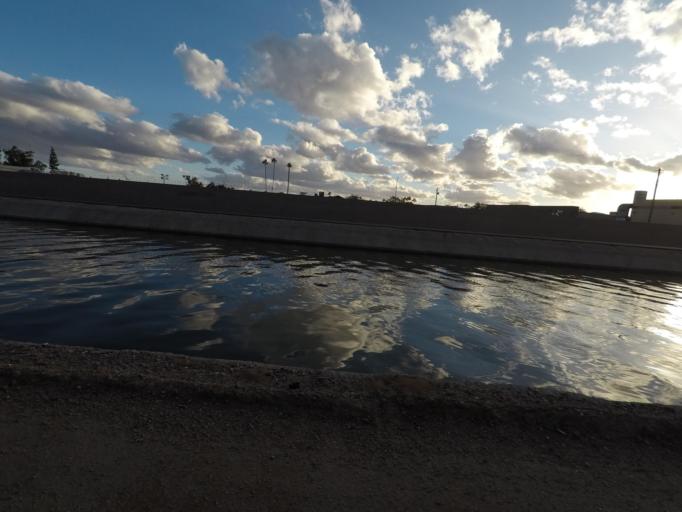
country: US
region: Arizona
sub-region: Maricopa County
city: Glendale
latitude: 33.4896
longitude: -112.1363
